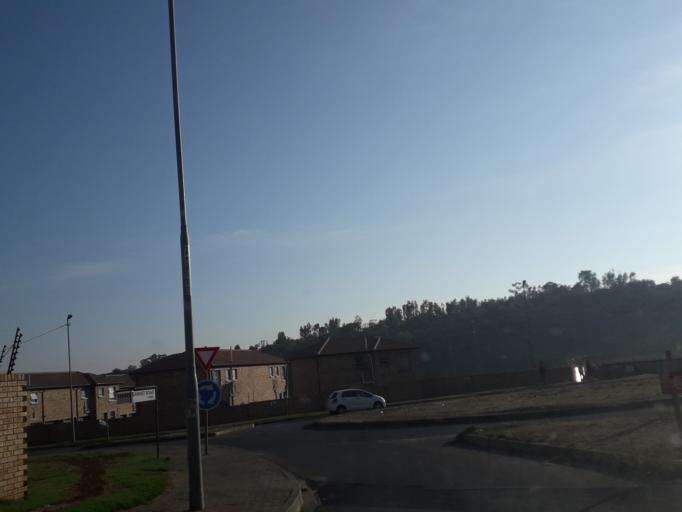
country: ZA
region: Gauteng
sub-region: City of Johannesburg Metropolitan Municipality
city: Roodepoort
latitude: -26.1067
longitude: 27.8890
